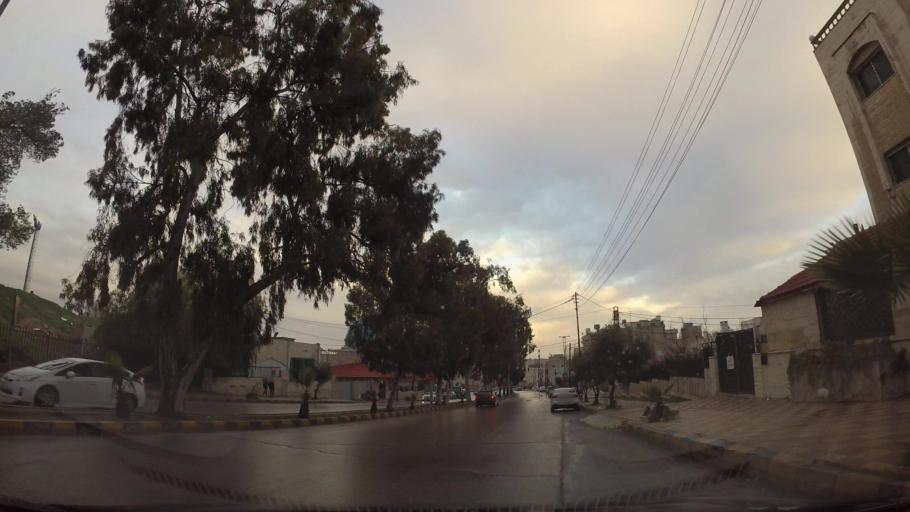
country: JO
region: Amman
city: Amman
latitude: 31.9789
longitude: 35.9093
